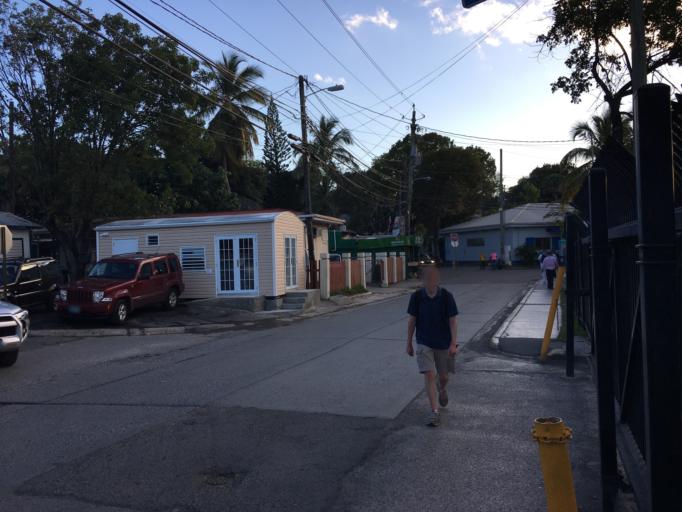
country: VI
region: Saint John Island
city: Cruz Bay
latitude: 18.3317
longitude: -64.7937
